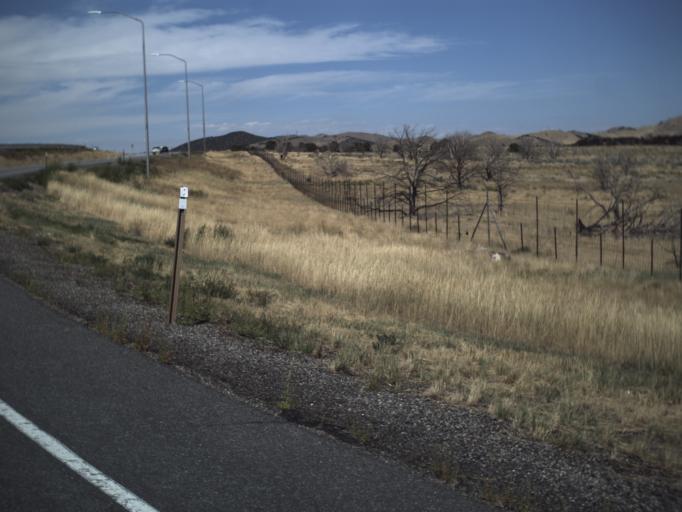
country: US
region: Utah
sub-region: Beaver County
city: Beaver
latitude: 38.5796
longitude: -112.6031
